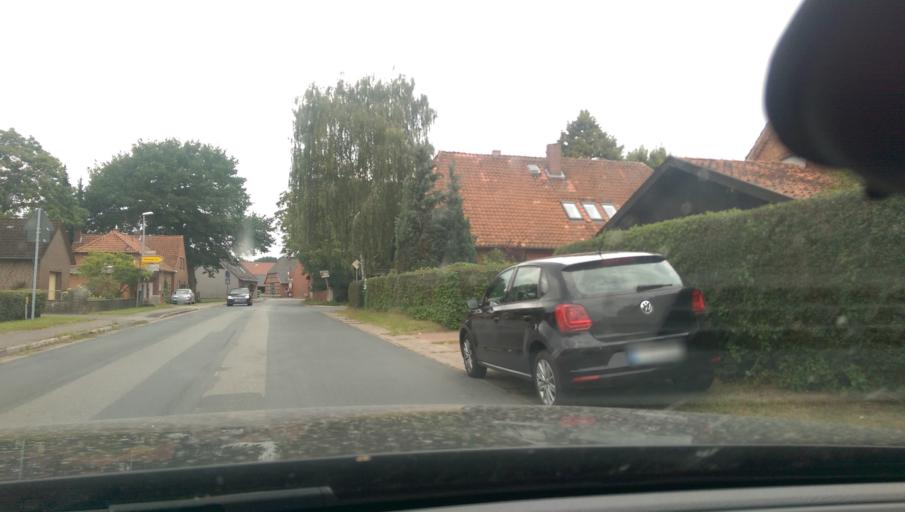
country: DE
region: Lower Saxony
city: Neustadt am Rubenberge
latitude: 52.5538
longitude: 9.5078
